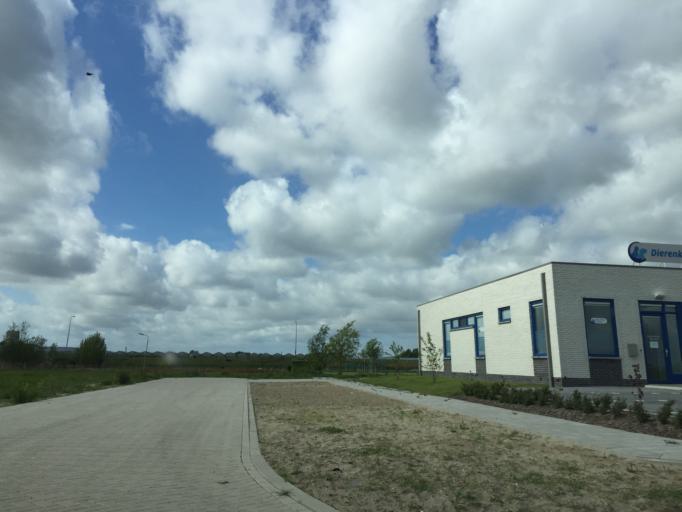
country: NL
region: South Holland
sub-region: Gemeente Pijnacker-Nootdorp
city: Pijnacker
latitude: 52.0308
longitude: 4.4447
